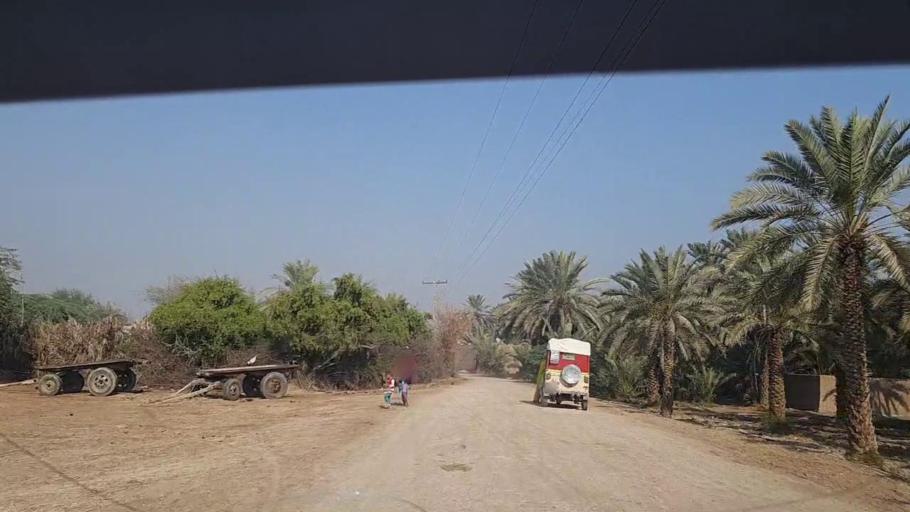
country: PK
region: Sindh
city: Khairpur
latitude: 27.4981
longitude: 68.7371
